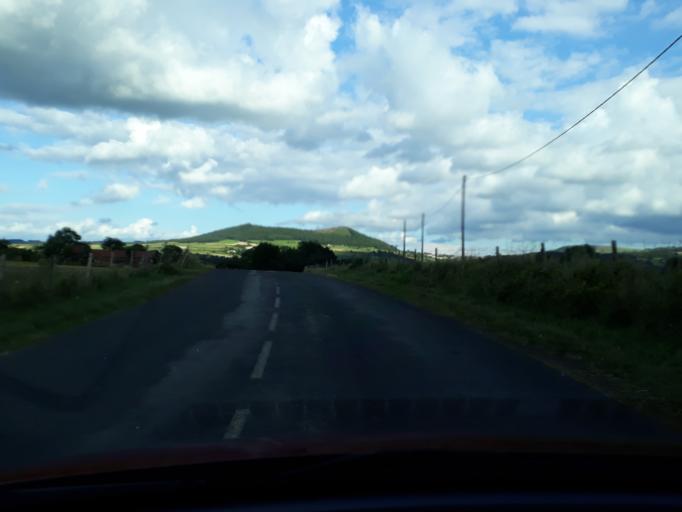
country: FR
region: Languedoc-Roussillon
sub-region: Departement de la Lozere
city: Langogne
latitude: 44.8222
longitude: 3.9261
